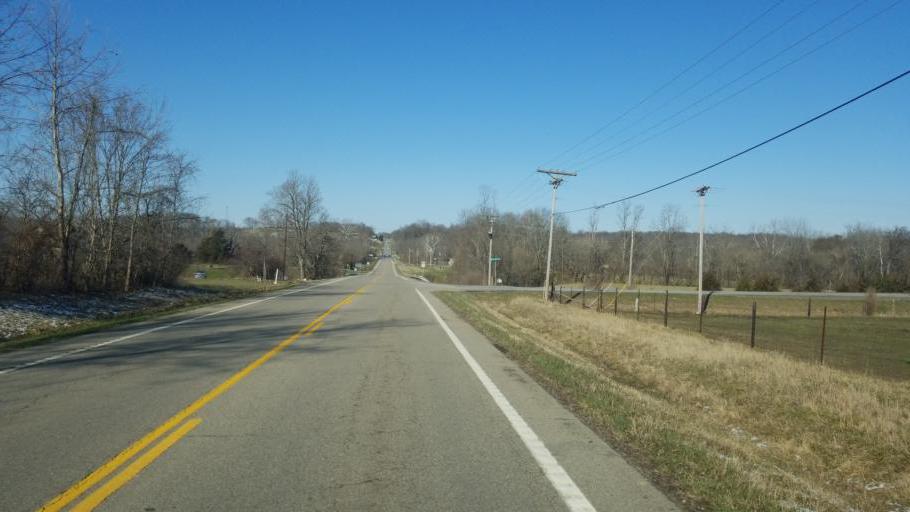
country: US
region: Ohio
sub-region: Highland County
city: Greenfield
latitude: 39.2311
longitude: -83.3393
